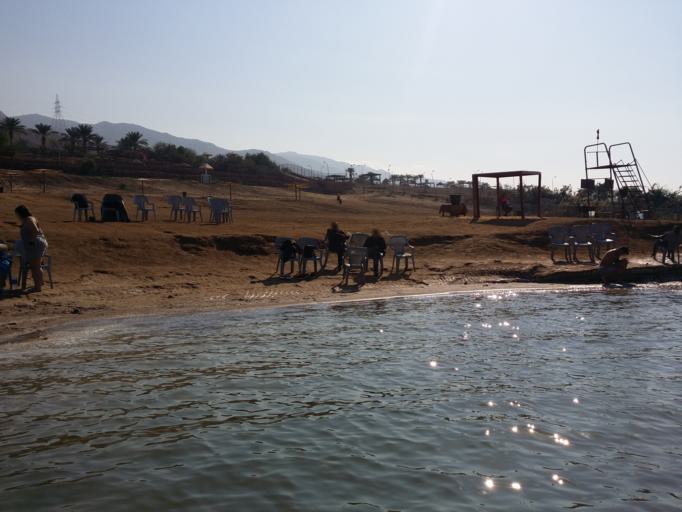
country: PS
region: West Bank
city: Jericho
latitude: 31.7013
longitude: 35.5813
